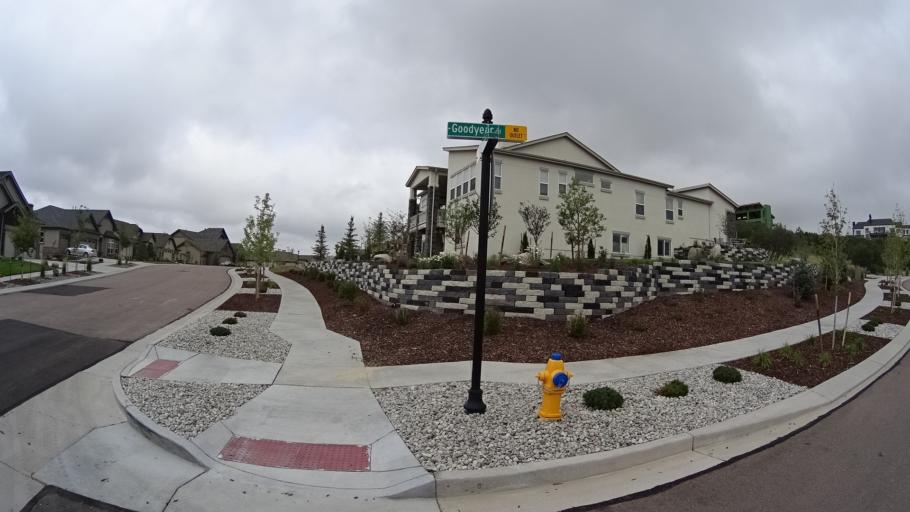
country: US
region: Colorado
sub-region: El Paso County
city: Gleneagle
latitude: 39.0141
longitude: -104.7922
